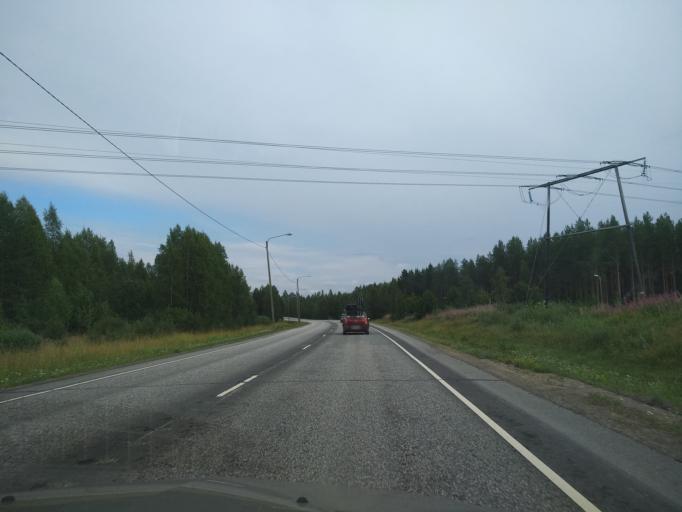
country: FI
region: Kainuu
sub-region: Kajaani
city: Paltamo
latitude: 64.4014
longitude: 27.8720
